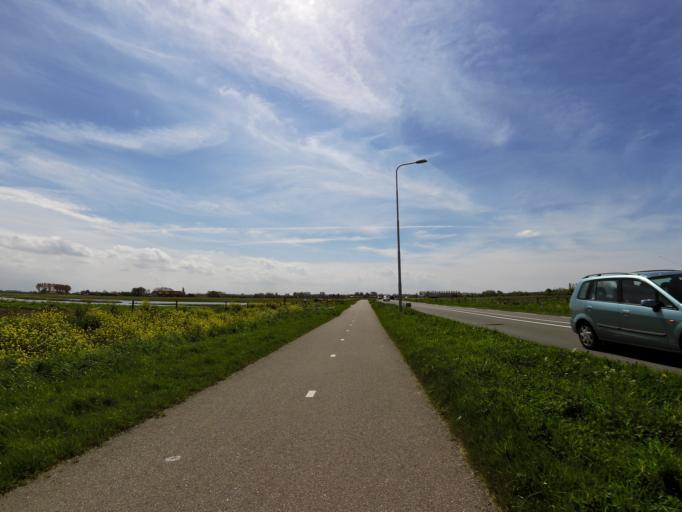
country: NL
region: South Holland
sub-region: Gemeente Hellevoetsluis
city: Nieuwenhoorn
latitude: 51.8868
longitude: 4.0967
